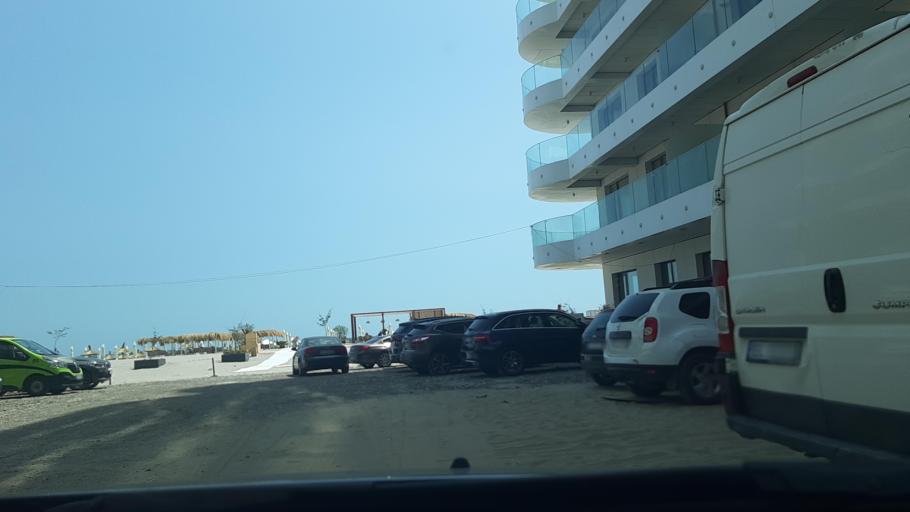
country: RO
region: Constanta
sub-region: Comuna Navodari
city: Navodari
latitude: 44.2766
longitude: 28.6208
